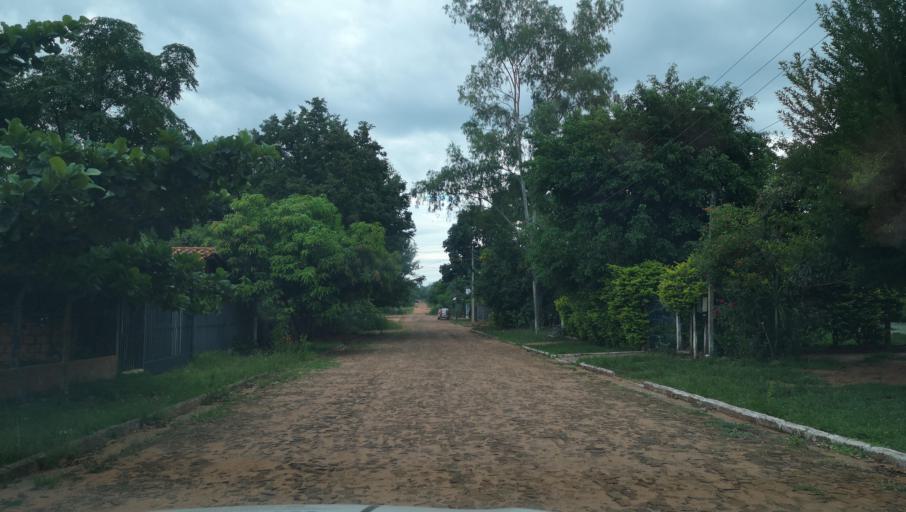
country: PY
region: San Pedro
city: Capiibary
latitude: -24.7271
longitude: -56.0198
